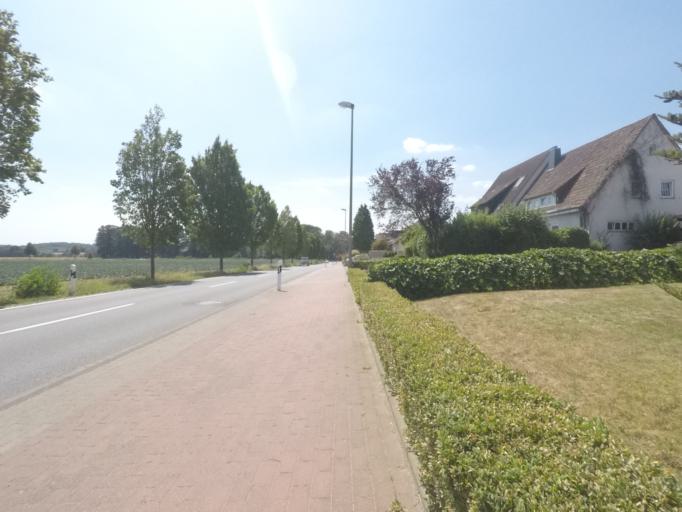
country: DE
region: North Rhine-Westphalia
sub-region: Regierungsbezirk Detmold
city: Hiddenhausen
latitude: 52.1190
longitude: 8.6121
